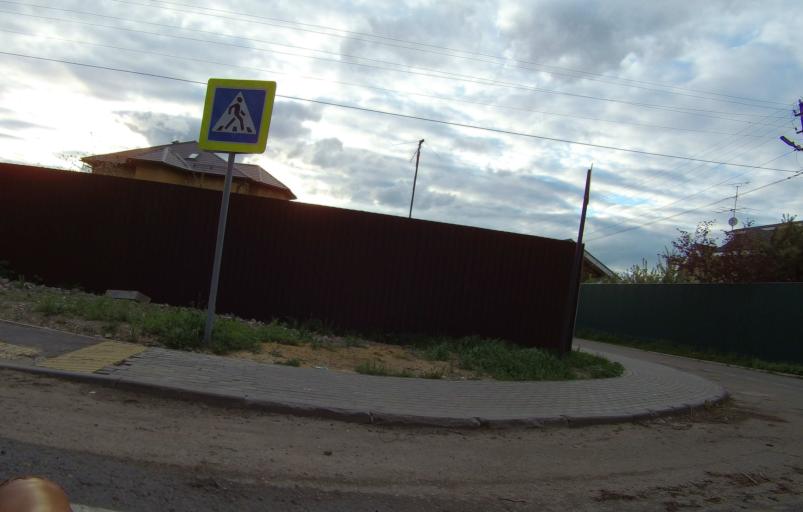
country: RU
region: Moskovskaya
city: Ramenskoye
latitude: 55.5791
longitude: 38.2548
